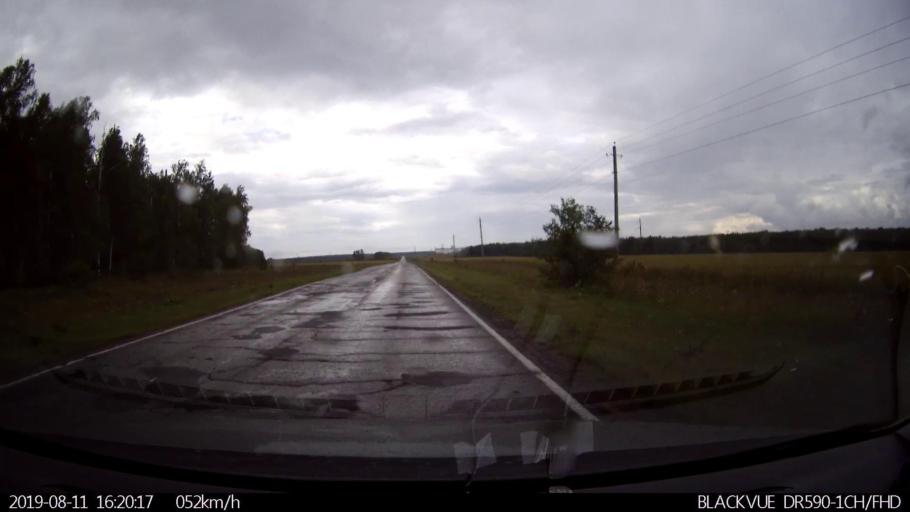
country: RU
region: Ulyanovsk
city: Mayna
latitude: 54.0705
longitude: 47.6037
